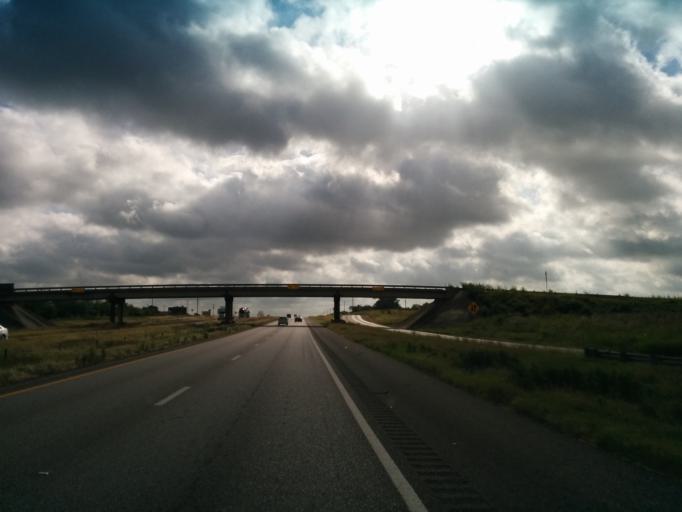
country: US
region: Texas
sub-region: Guadalupe County
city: Marion
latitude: 29.5076
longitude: -98.1690
